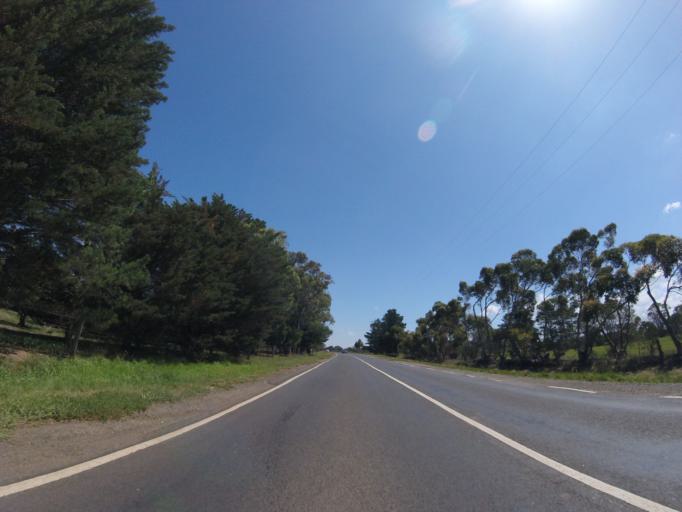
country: AU
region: Victoria
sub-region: Hume
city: Diggers Rest
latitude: -37.6331
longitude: 144.7401
